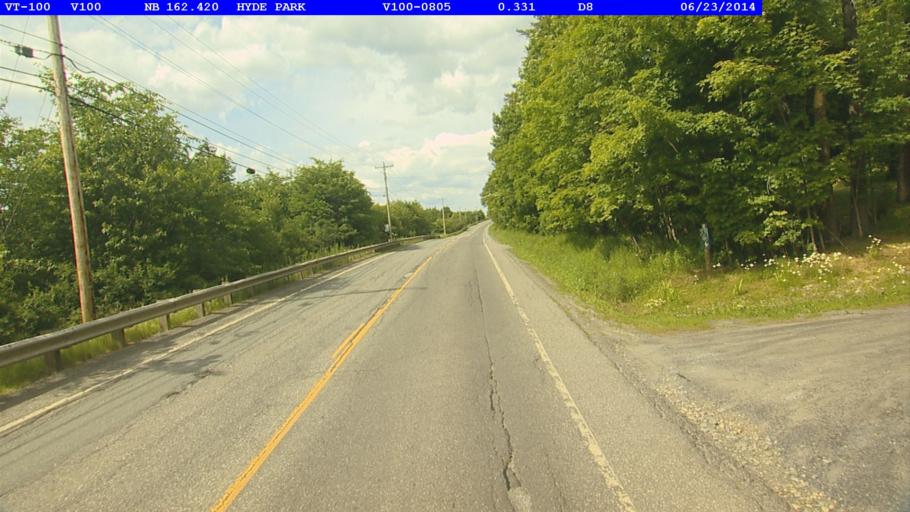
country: US
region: Vermont
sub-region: Lamoille County
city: Hyde Park
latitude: 44.6021
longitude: -72.6149
